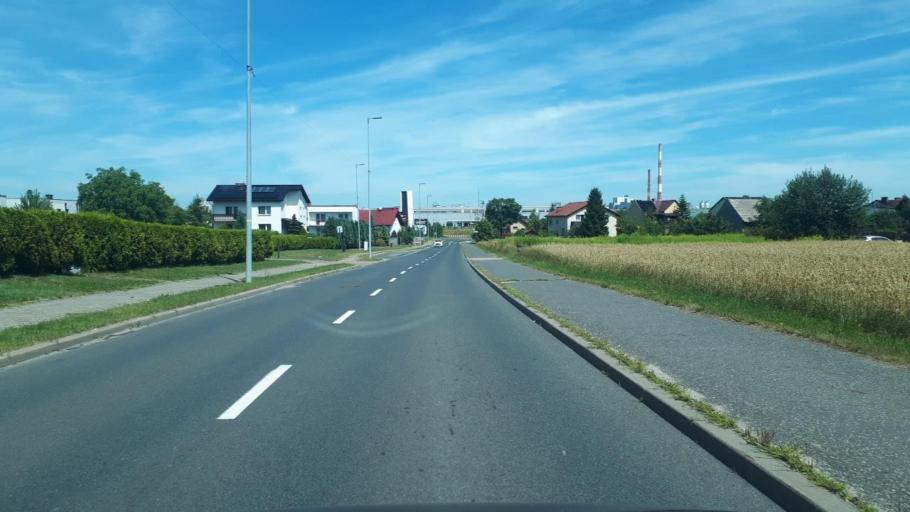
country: PL
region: Silesian Voivodeship
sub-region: Tychy
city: Cielmice
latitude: 50.0893
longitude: 19.0085
